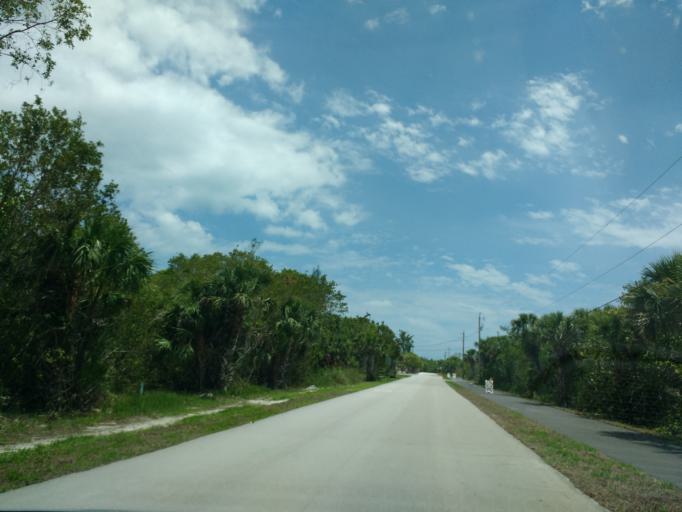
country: US
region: Florida
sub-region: Lee County
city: Saint James City
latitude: 26.4633
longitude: -82.1526
